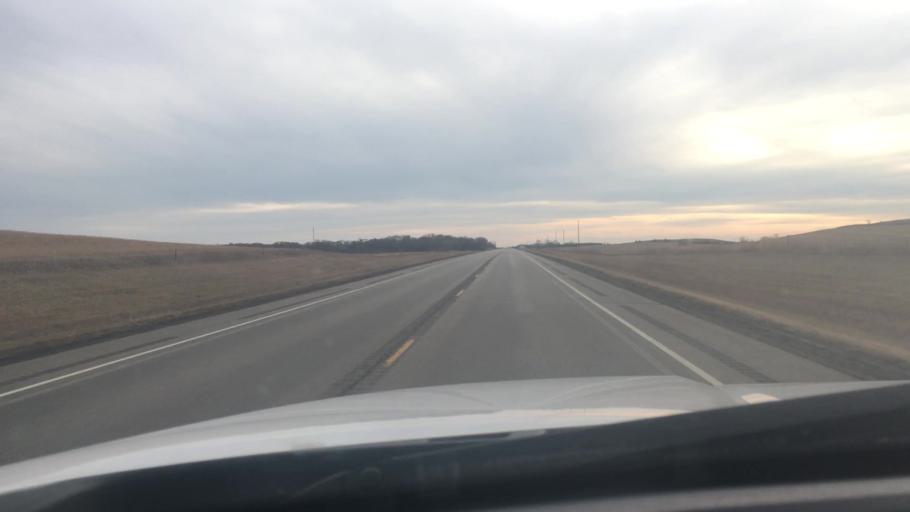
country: US
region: Minnesota
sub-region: Otter Tail County
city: Perham
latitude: 46.3380
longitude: -95.7185
